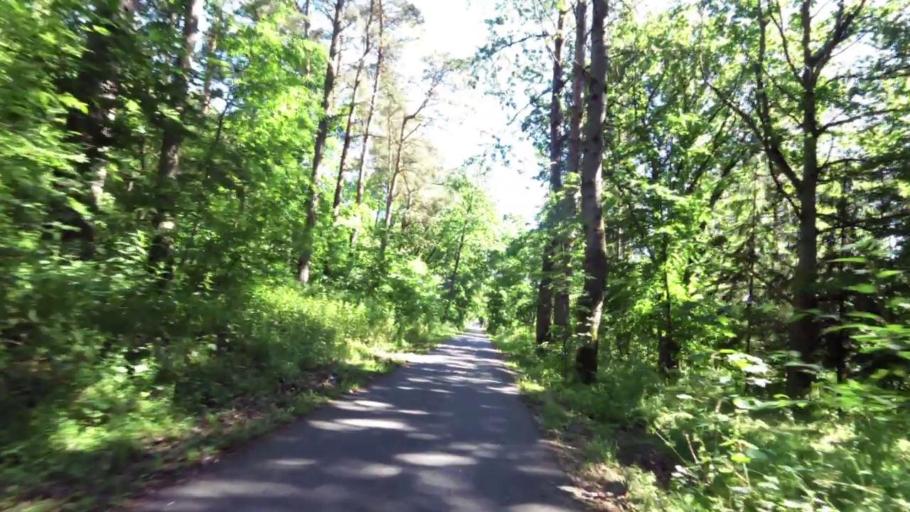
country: PL
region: West Pomeranian Voivodeship
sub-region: Powiat bialogardzki
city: Karlino
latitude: 54.0513
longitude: 15.8773
